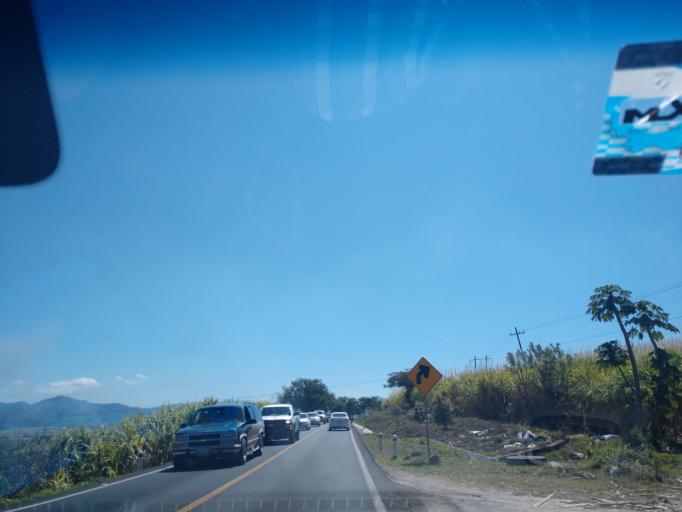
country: MX
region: Nayarit
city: Xalisco
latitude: 21.3897
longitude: -104.8921
